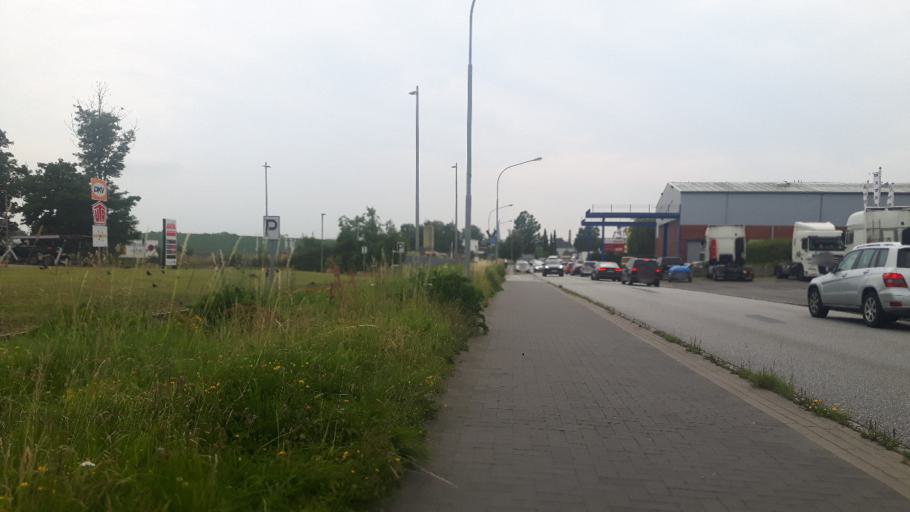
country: DE
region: Schleswig-Holstein
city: Luebeck
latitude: 53.8893
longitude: 10.6914
